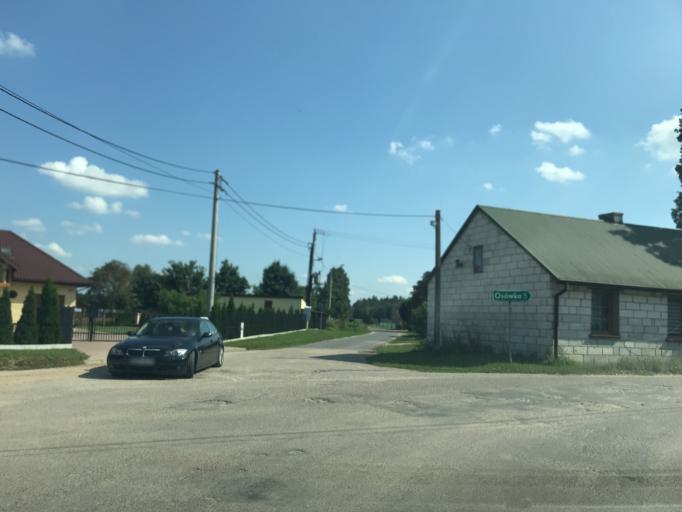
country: PL
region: Masovian Voivodeship
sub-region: Powiat zurominski
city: Zuromin
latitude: 53.1513
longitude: 19.9356
